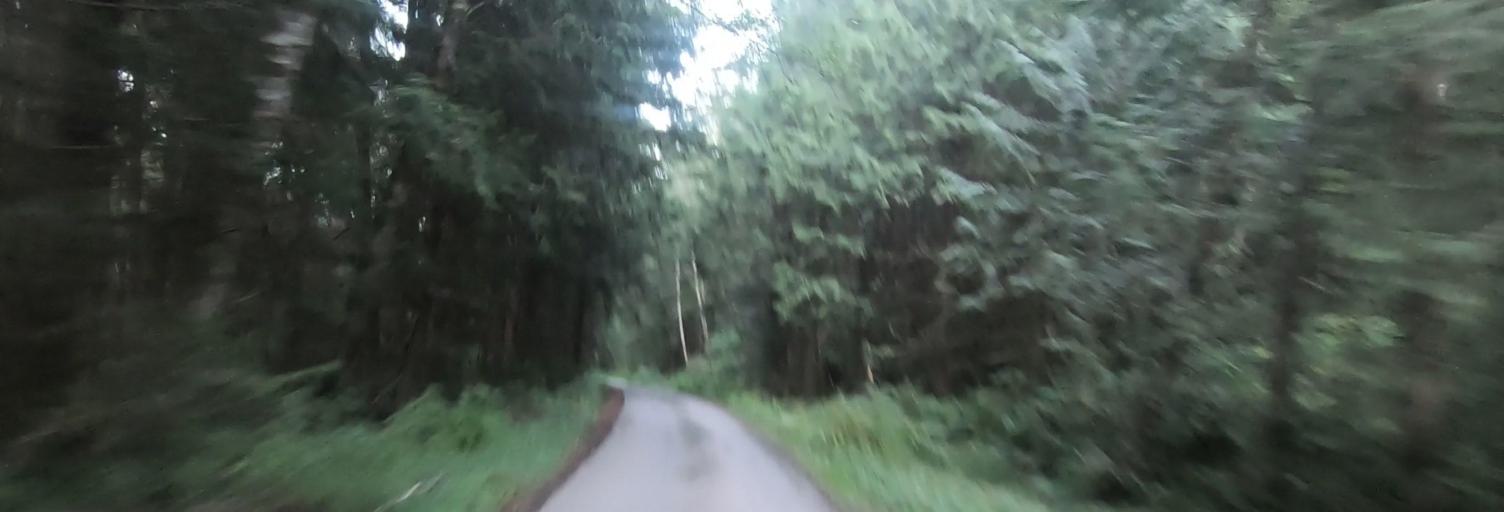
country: US
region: Washington
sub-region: Whatcom County
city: Peaceful Valley
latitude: 48.9474
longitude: -121.9355
